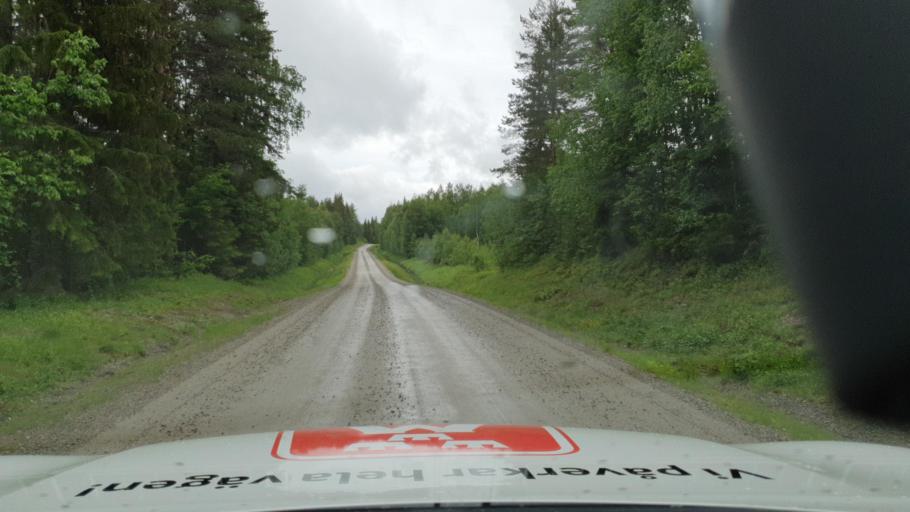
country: SE
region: Vaesterbotten
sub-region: Dorotea Kommun
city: Dorotea
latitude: 64.0521
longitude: 16.7279
